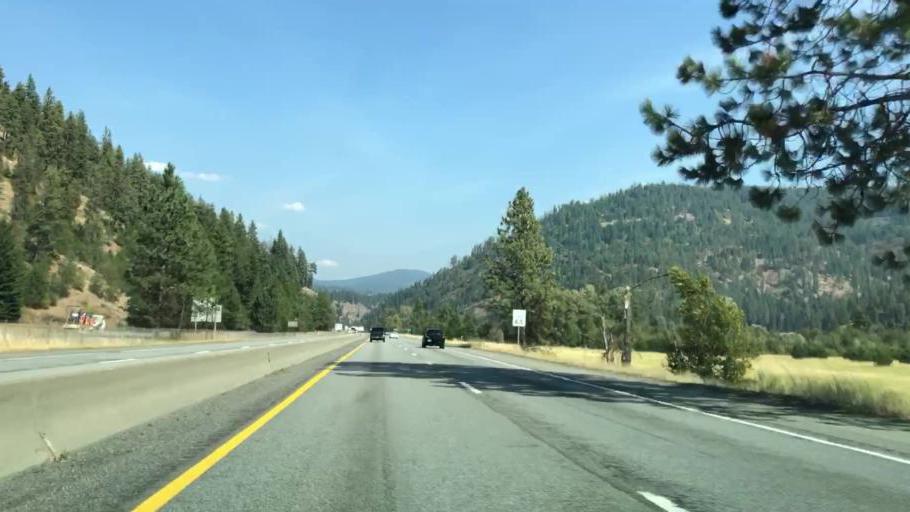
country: US
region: Idaho
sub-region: Kootenai County
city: Coeur d'Alene
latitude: 47.6251
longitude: -116.6396
